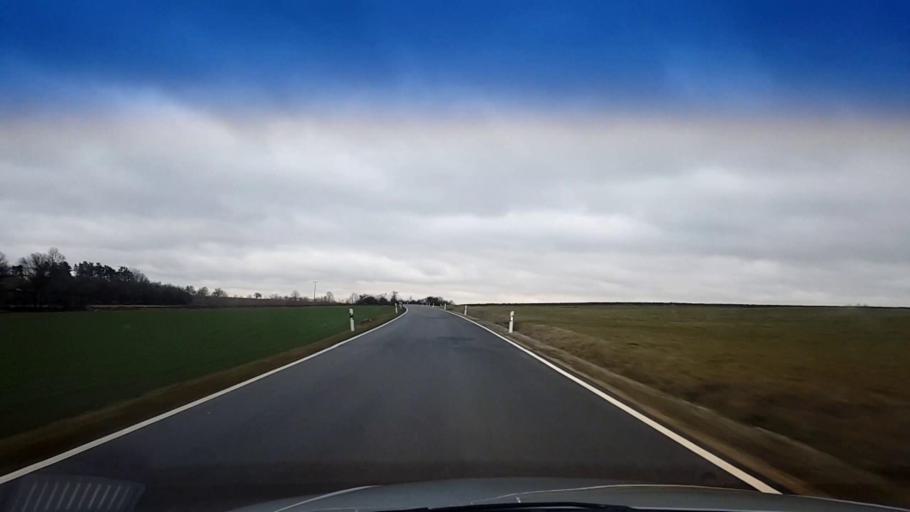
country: DE
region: Bavaria
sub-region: Upper Franconia
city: Wattendorf
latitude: 50.0337
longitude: 11.0645
